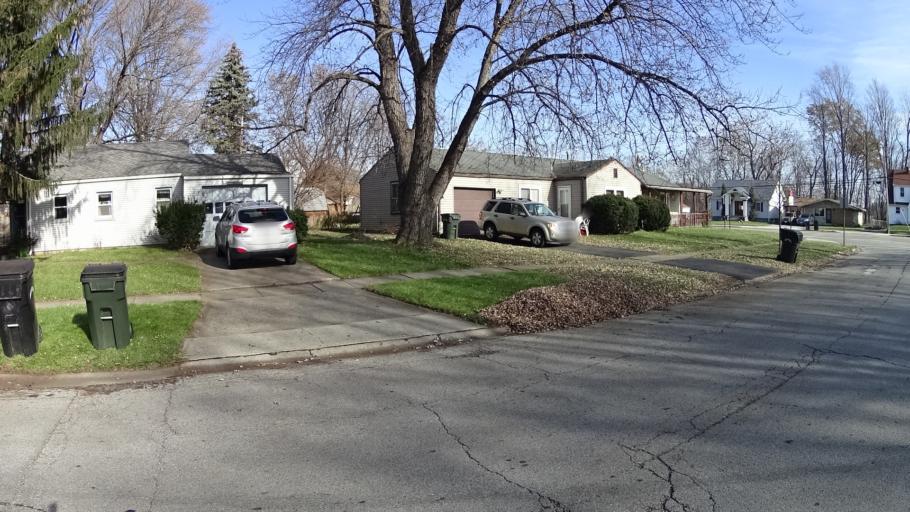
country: US
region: Ohio
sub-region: Lorain County
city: Elyria
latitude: 41.3838
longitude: -82.1062
